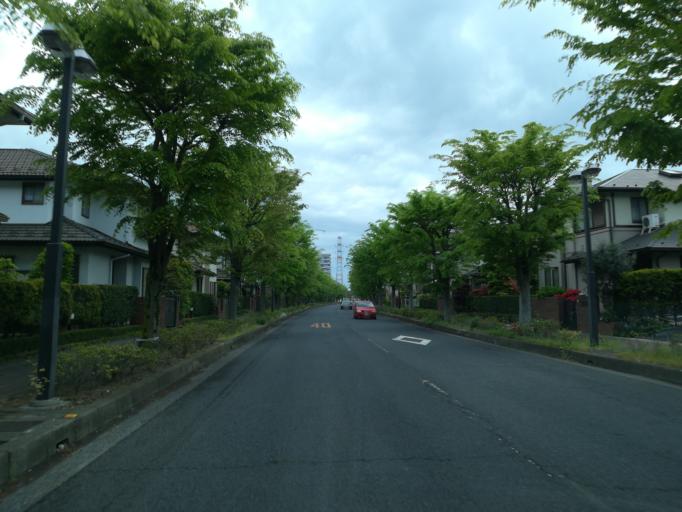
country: JP
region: Saitama
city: Shiraoka
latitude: 36.0354
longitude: 139.6745
